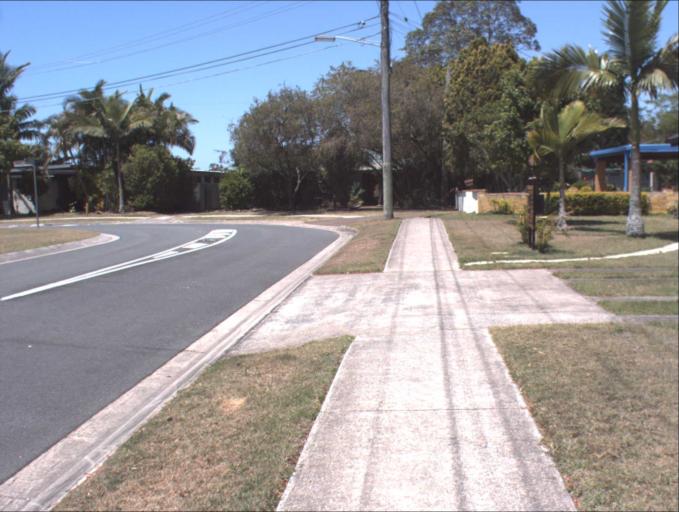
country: AU
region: Queensland
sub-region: Logan
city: Rochedale South
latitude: -27.5918
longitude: 153.1256
